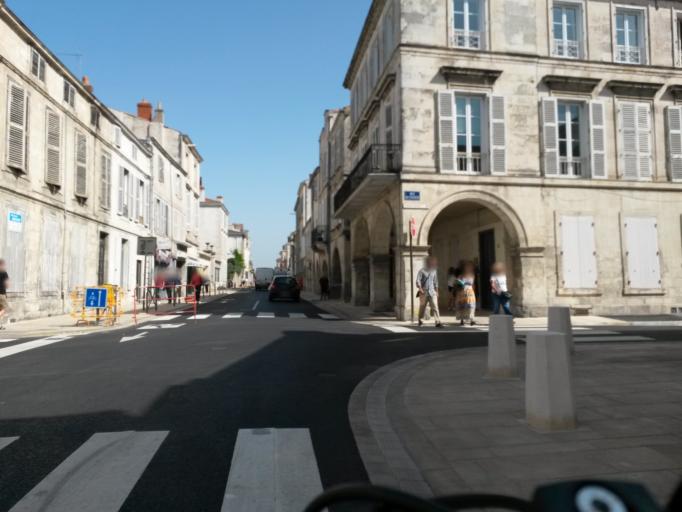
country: FR
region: Poitou-Charentes
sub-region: Departement de la Charente-Maritime
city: La Rochelle
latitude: 46.1635
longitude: -1.1521
